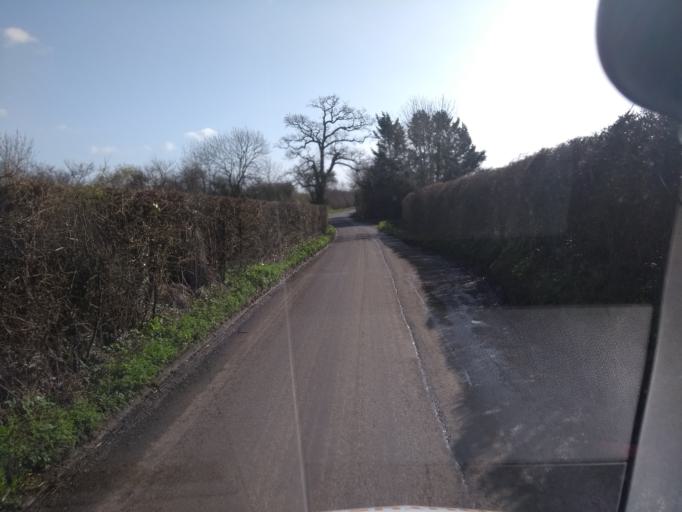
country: GB
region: England
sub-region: Somerset
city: Curry Rivel
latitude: 50.9911
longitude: -2.8564
